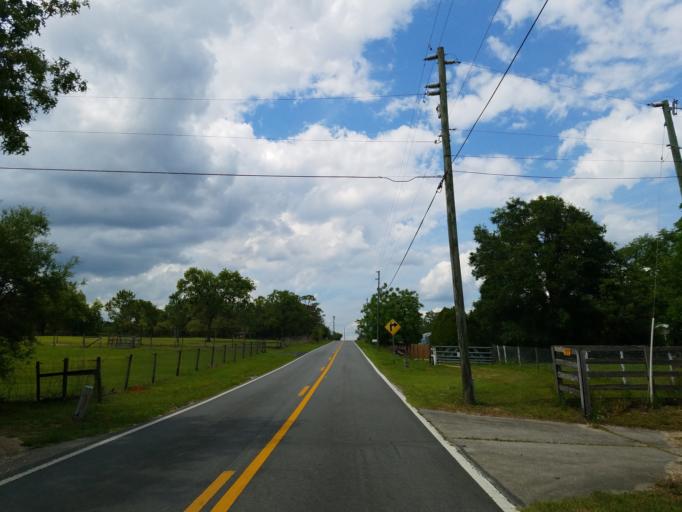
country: US
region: Florida
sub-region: Hernando County
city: Hill 'n Dale
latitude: 28.5335
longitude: -82.2759
